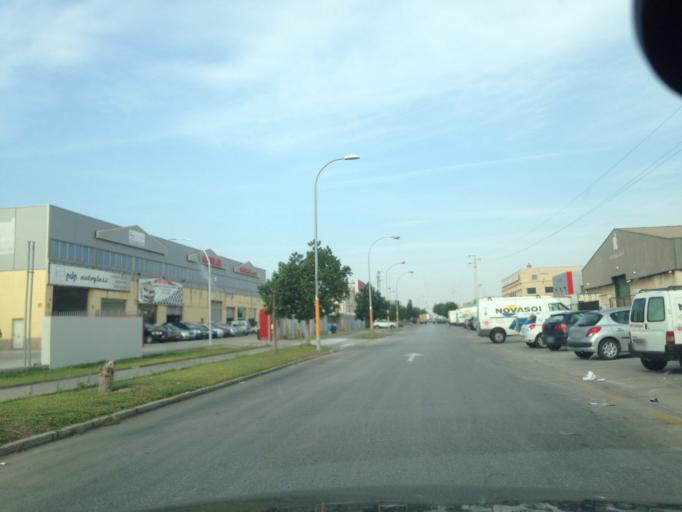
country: ES
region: Andalusia
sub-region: Provincia de Malaga
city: Malaga
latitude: 36.6881
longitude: -4.4708
